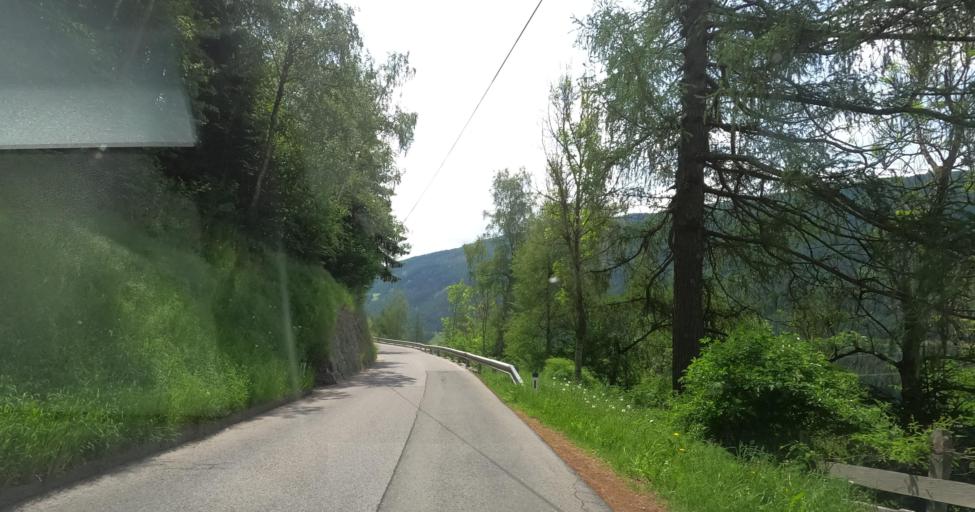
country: AT
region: Tyrol
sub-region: Politischer Bezirk Innsbruck Land
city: Ellbogen
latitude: 47.1722
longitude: 11.4414
